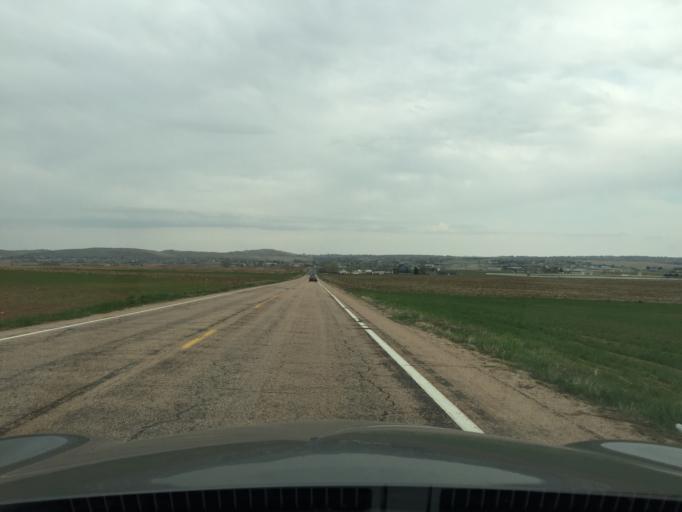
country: US
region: Colorado
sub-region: Boulder County
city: Lafayette
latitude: 40.0149
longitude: -105.0707
